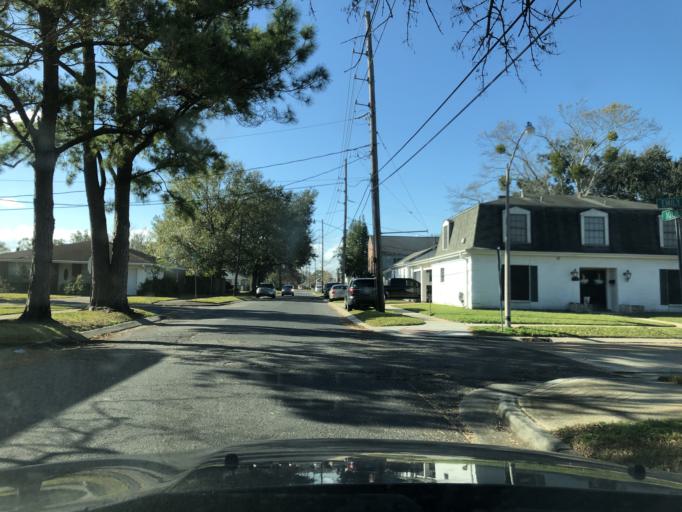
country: US
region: Louisiana
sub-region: Jefferson Parish
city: Metairie Terrace
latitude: 29.9878
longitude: -90.1651
